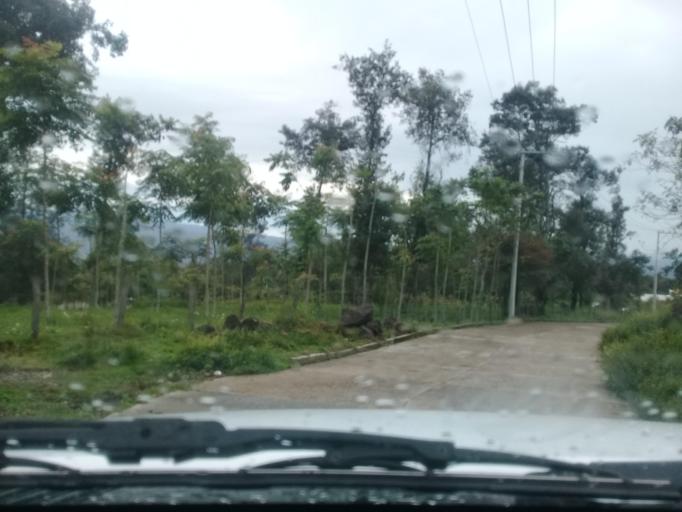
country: MX
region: Veracruz
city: Rafael Lucio
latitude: 19.6165
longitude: -96.9940
